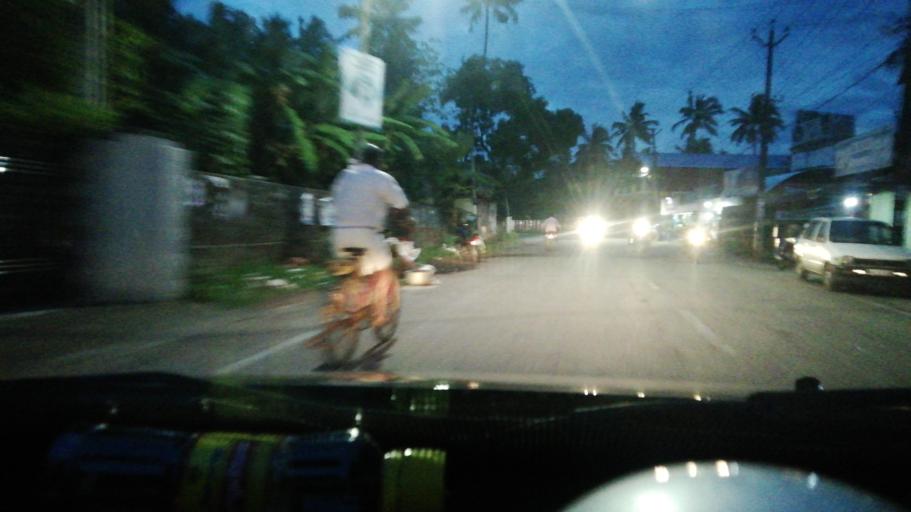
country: IN
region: Kerala
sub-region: Thiruvananthapuram
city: Paravur
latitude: 8.8124
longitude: 76.6803
